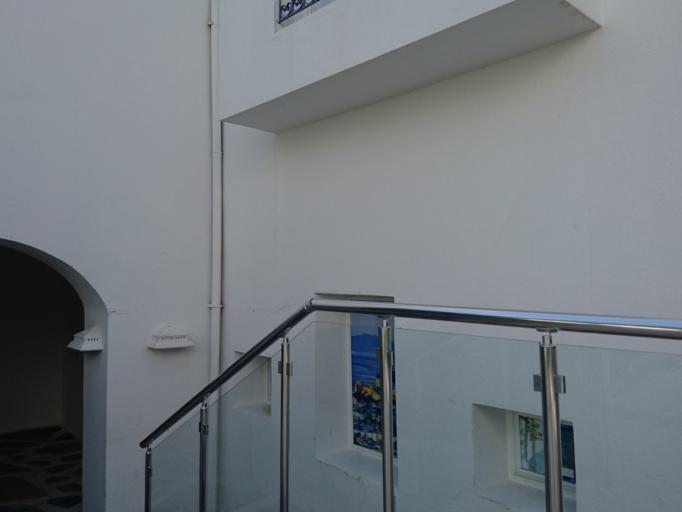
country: TR
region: Mugla
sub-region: Bodrum
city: Bodrum
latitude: 37.0283
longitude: 27.4156
